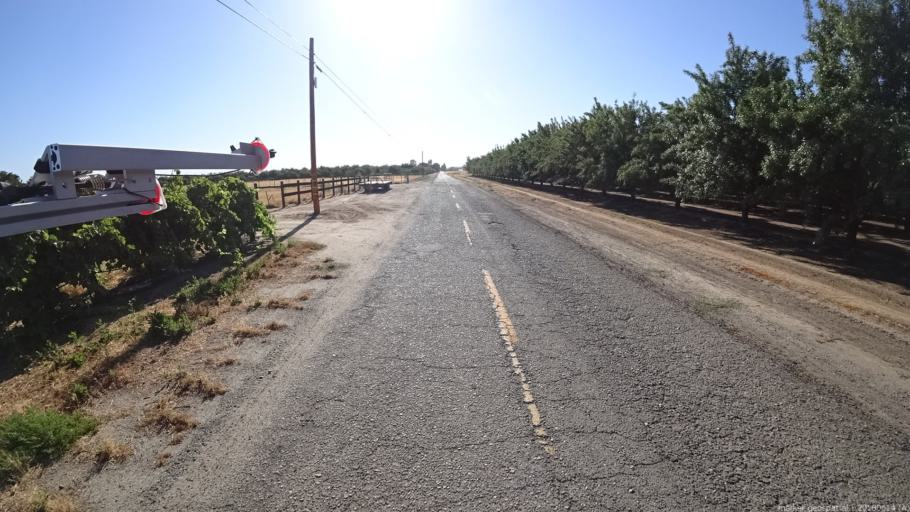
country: US
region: California
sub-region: Madera County
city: Madera
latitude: 36.9311
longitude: -120.1211
